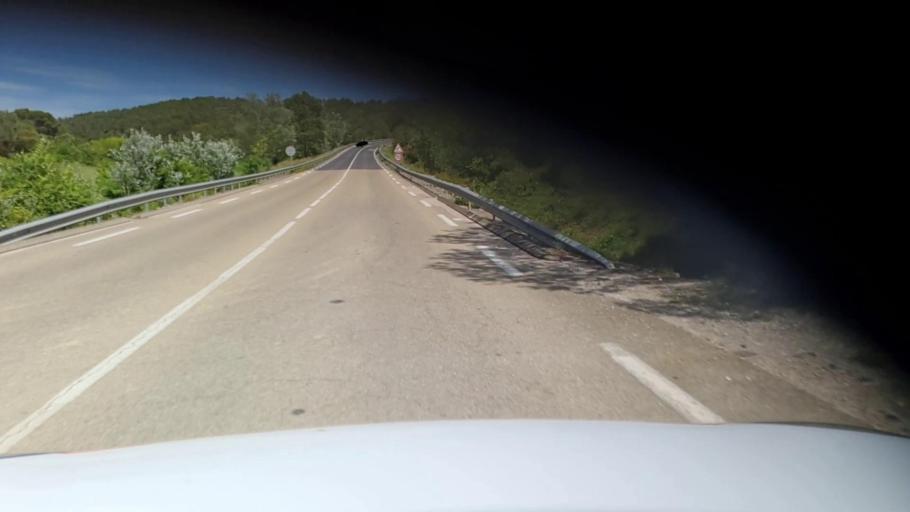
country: FR
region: Languedoc-Roussillon
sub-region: Departement du Gard
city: Saint-Mamert-du-Gard
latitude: 43.8597
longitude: 4.1398
